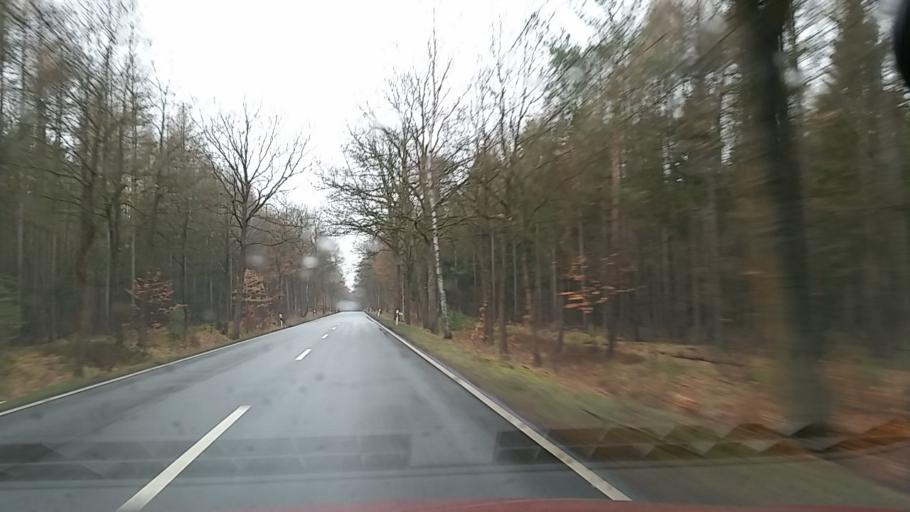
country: DE
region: Lower Saxony
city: Sprakensehl
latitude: 52.7874
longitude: 10.3974
